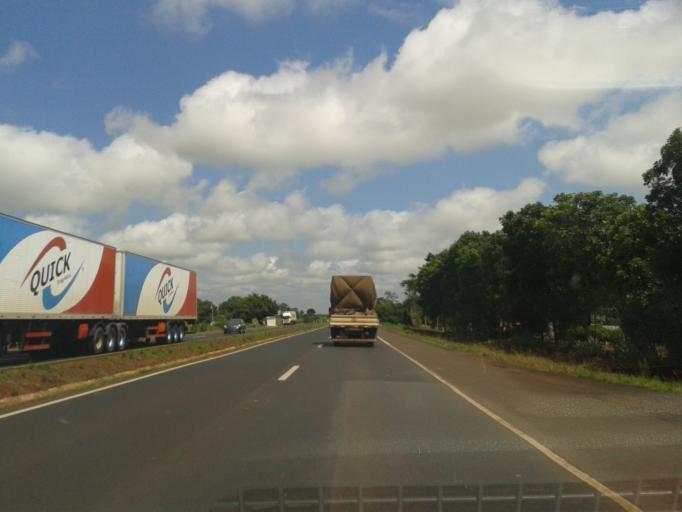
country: BR
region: Minas Gerais
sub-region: Centralina
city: Centralina
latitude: -18.7007
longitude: -49.1439
